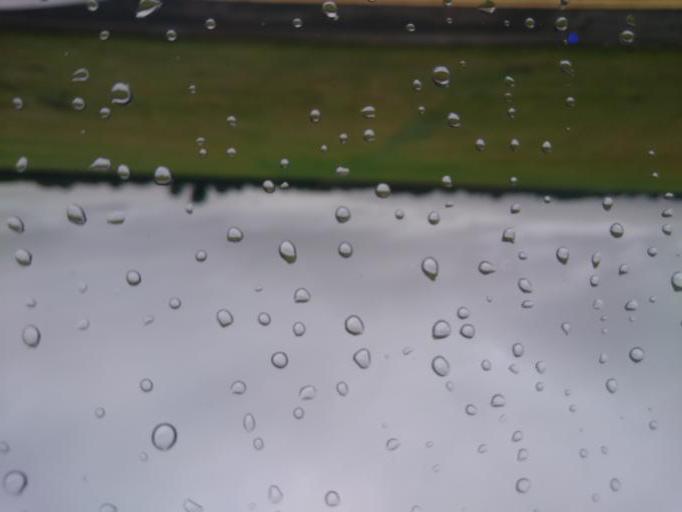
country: IE
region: Leinster
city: Ballymun
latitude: 53.4237
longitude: -6.2906
